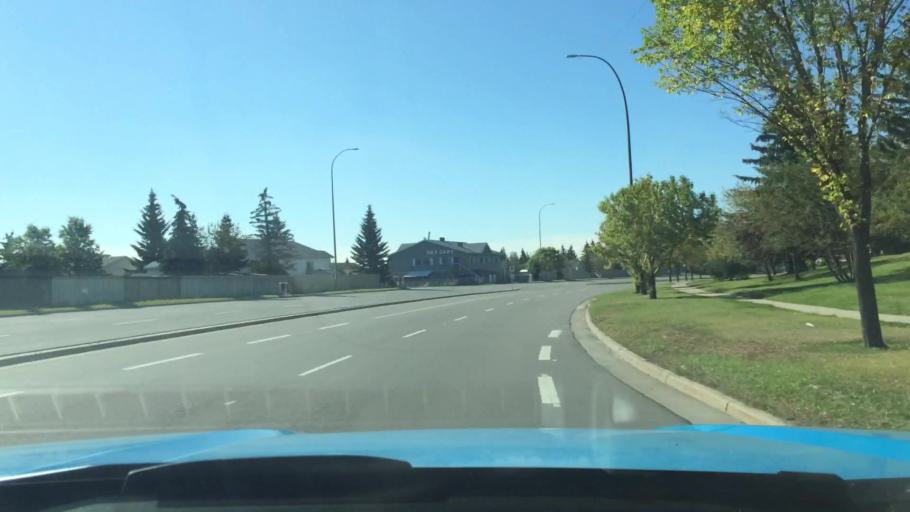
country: CA
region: Alberta
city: Calgary
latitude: 51.1171
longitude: -114.0526
